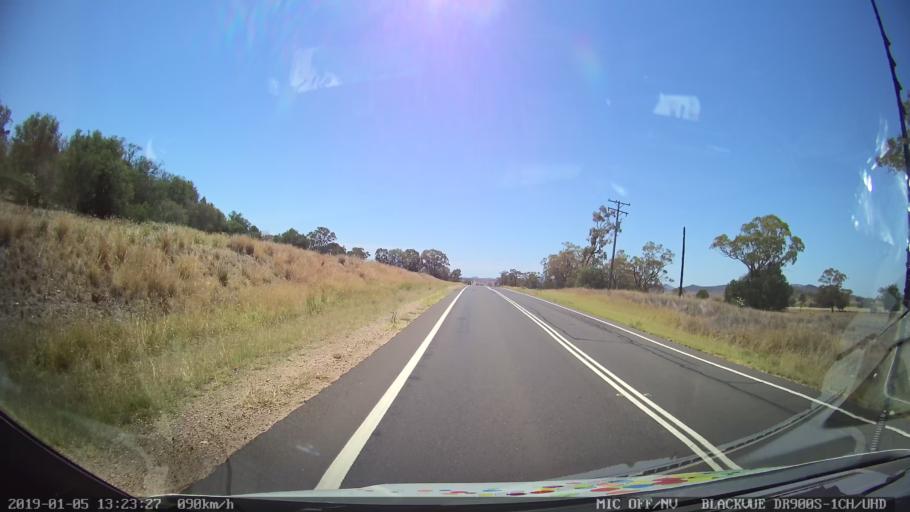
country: AU
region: New South Wales
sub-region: Gunnedah
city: Gunnedah
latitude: -31.0778
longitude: 149.9754
